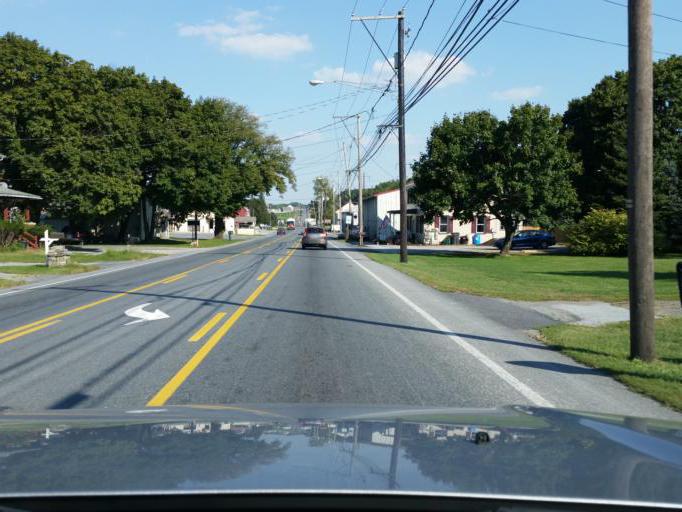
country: US
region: Pennsylvania
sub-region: Lancaster County
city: Intercourse
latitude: 40.0011
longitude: -76.0829
